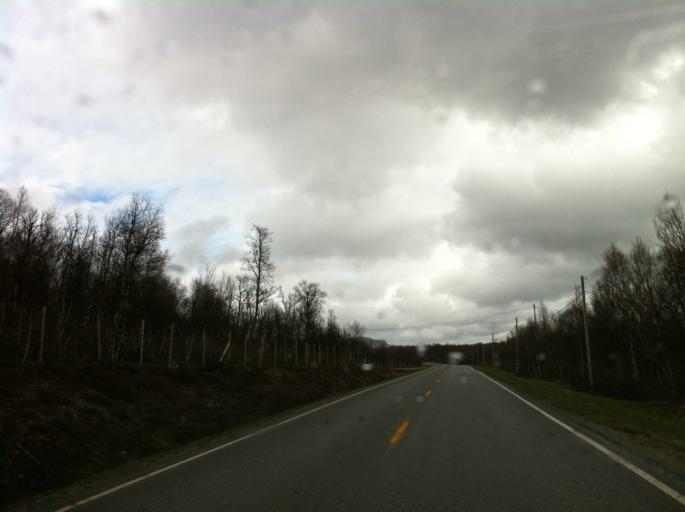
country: NO
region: Sor-Trondelag
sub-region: Tydal
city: Aas
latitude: 62.6407
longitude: 11.8897
